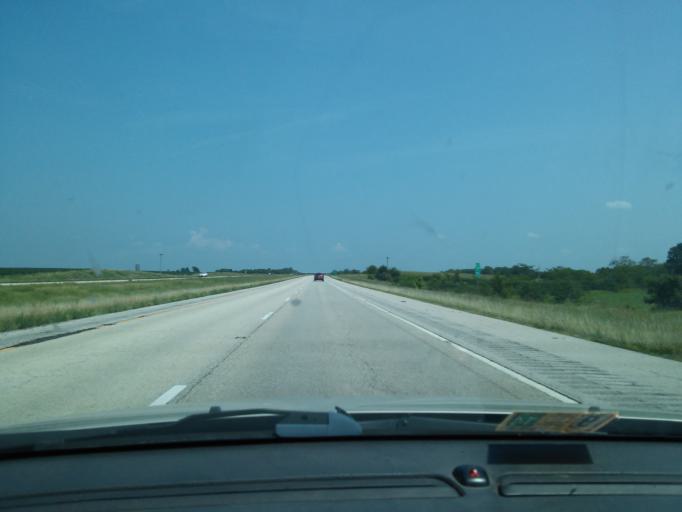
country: US
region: Illinois
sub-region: Sangamon County
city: New Berlin
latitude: 39.7368
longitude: -90.0566
